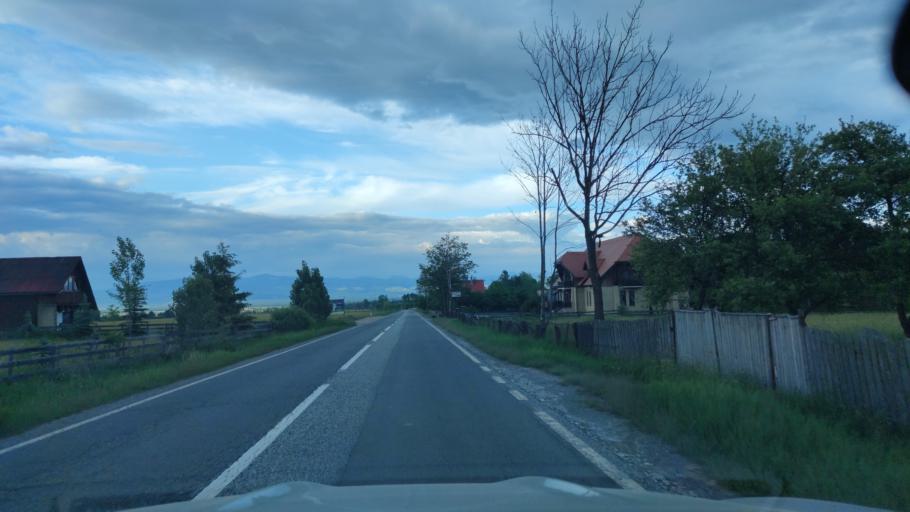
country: RO
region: Harghita
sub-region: Comuna Joseni
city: Joseni
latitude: 46.6792
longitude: 25.3970
